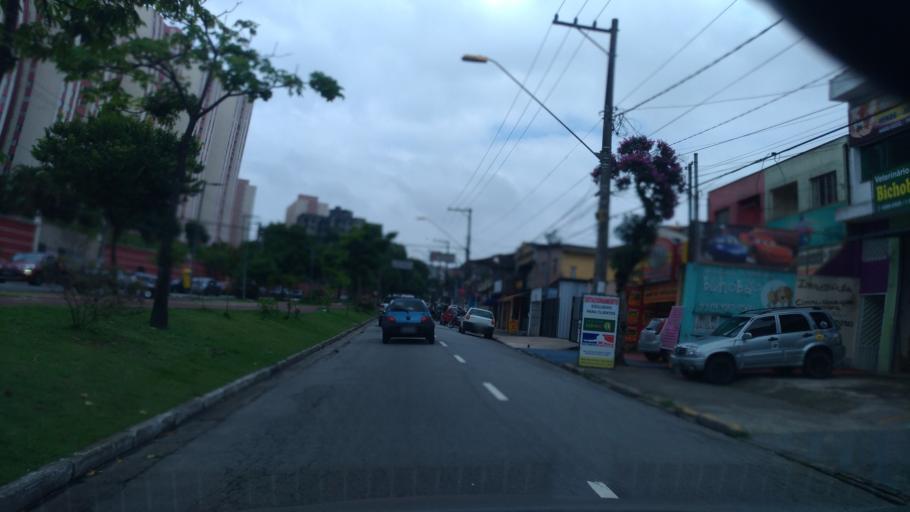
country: BR
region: Sao Paulo
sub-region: Santo Andre
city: Santo Andre
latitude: -23.6942
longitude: -46.5111
